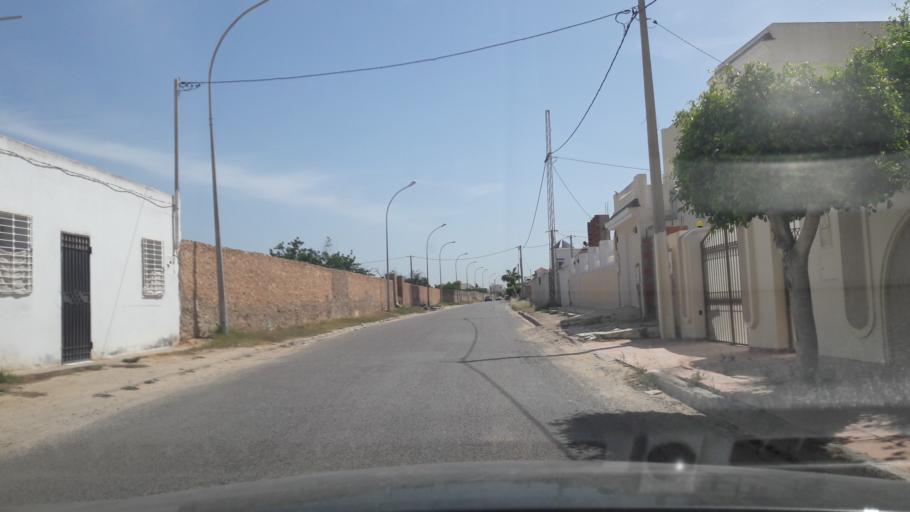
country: TN
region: Safaqis
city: Sfax
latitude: 34.7904
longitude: 10.7523
